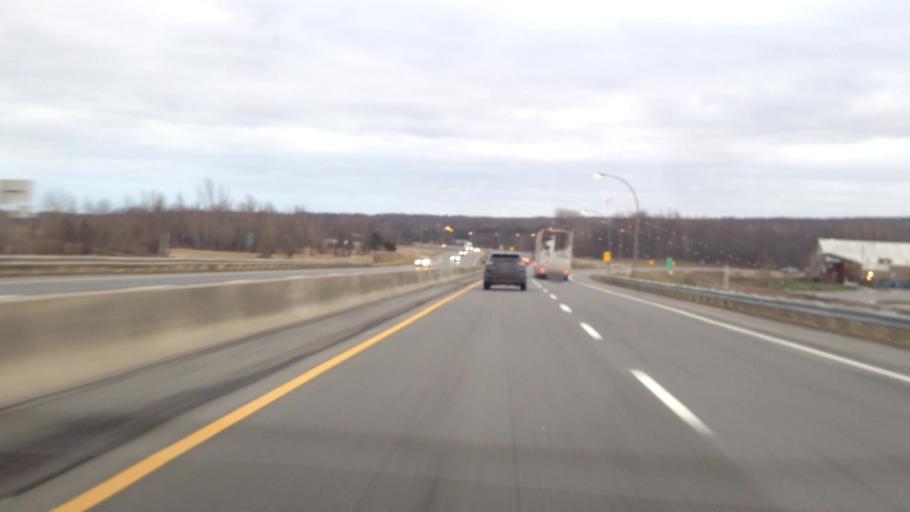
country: CA
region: Quebec
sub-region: Monteregie
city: Rigaud
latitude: 45.4792
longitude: -74.2847
